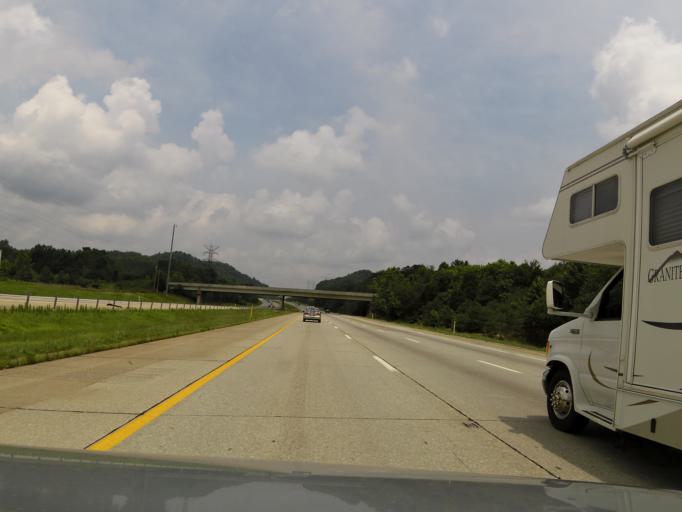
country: US
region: Kentucky
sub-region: Bullitt County
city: Lebanon Junction
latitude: 37.8702
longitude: -85.7040
